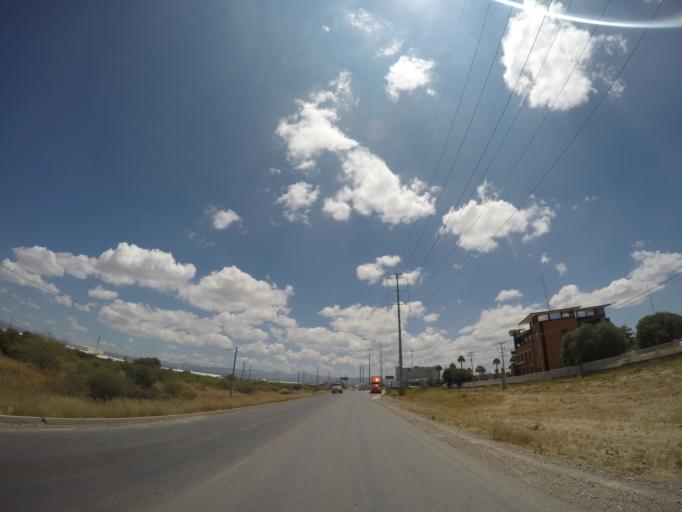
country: MX
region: San Luis Potosi
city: La Pila
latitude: 22.0425
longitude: -100.8953
